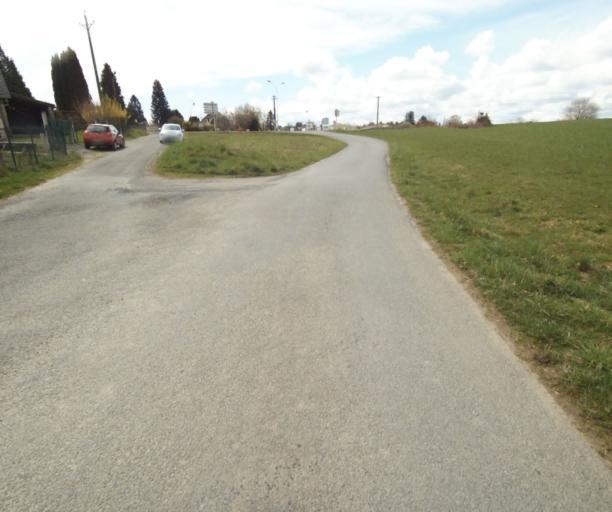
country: FR
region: Limousin
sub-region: Departement de la Correze
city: Egletons
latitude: 45.3584
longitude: 1.9801
